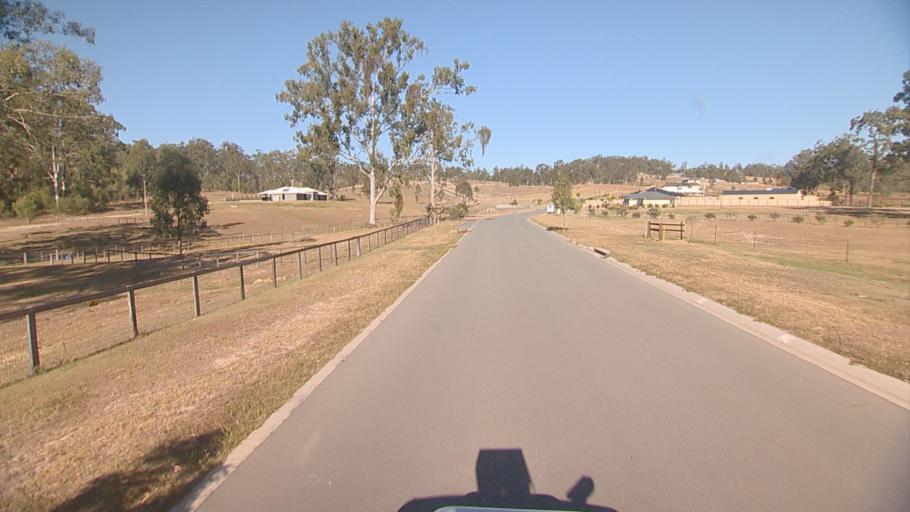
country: AU
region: Queensland
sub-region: Logan
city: Cedar Vale
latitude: -27.8695
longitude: 153.0554
